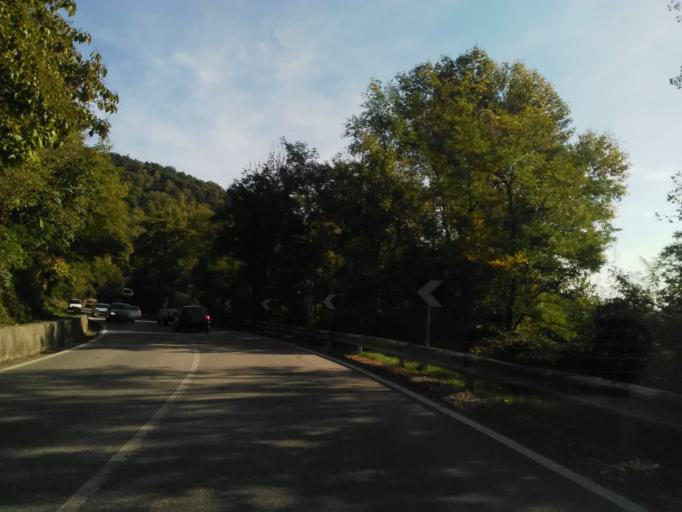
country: IT
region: Piedmont
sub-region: Provincia di Vercelli
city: Borgosesia
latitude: 45.7010
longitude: 8.2816
